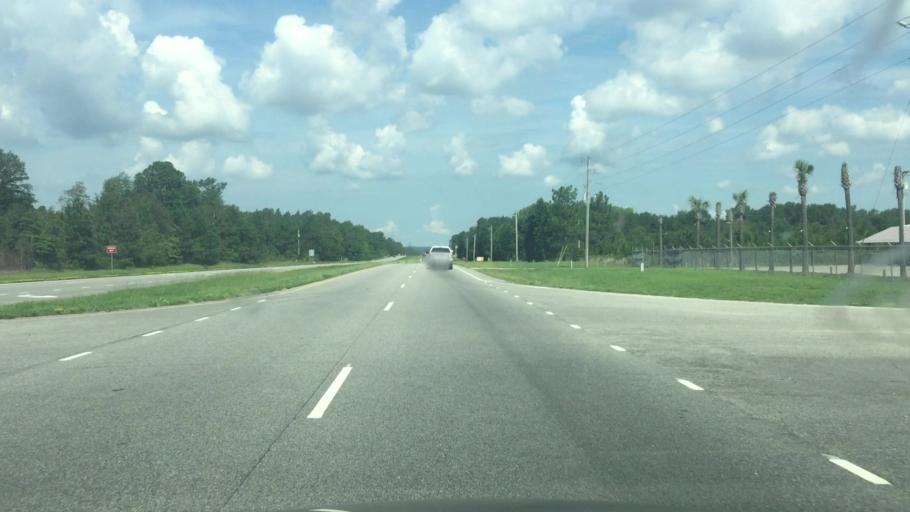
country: US
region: North Carolina
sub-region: Scotland County
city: Laurel Hill
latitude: 34.8372
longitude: -79.5979
